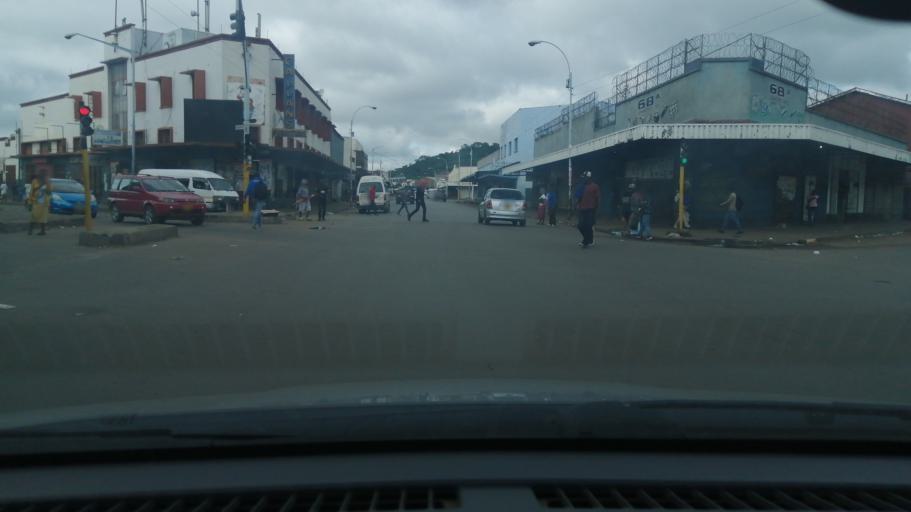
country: ZW
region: Harare
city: Harare
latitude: -17.8378
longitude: 31.0441
